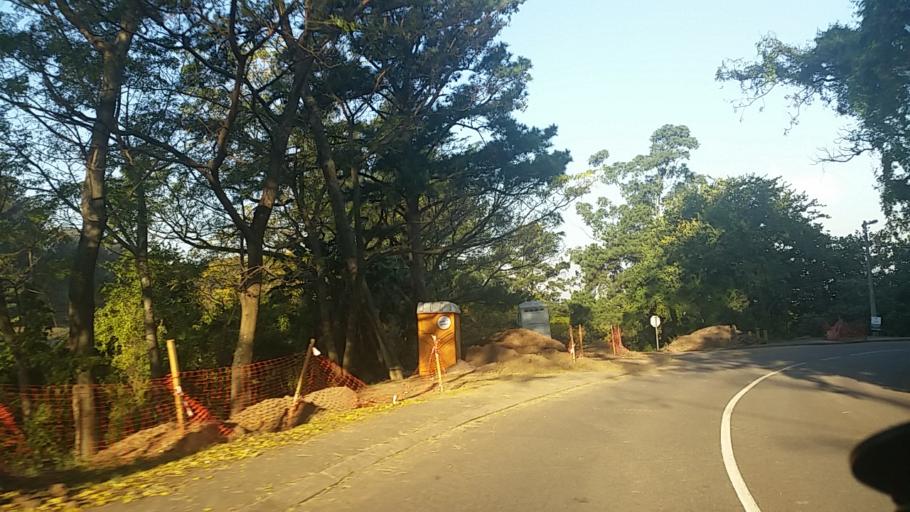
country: ZA
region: KwaZulu-Natal
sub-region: eThekwini Metropolitan Municipality
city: Berea
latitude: -29.8421
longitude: 30.9173
